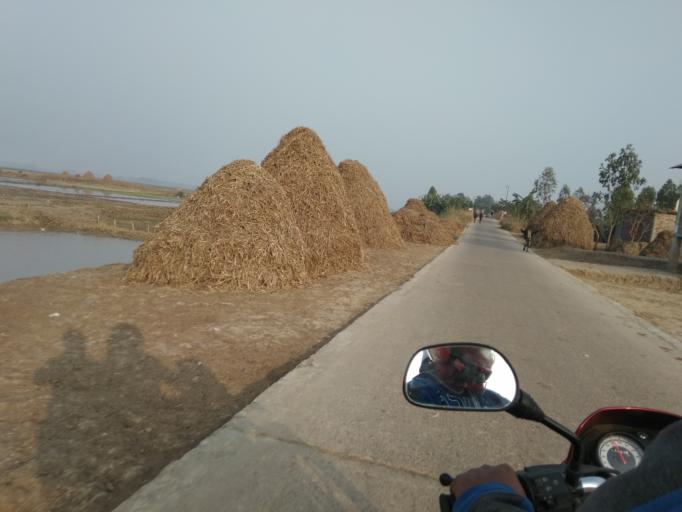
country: BD
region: Rajshahi
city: Ishurdi
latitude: 24.4811
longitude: 89.2321
